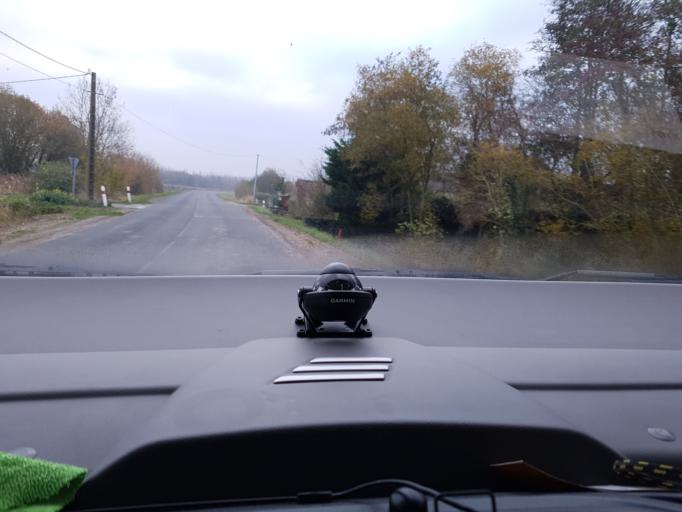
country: FR
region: Picardie
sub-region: Departement de la Somme
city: Cayeux-sur-Mer
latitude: 50.1468
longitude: 1.5075
